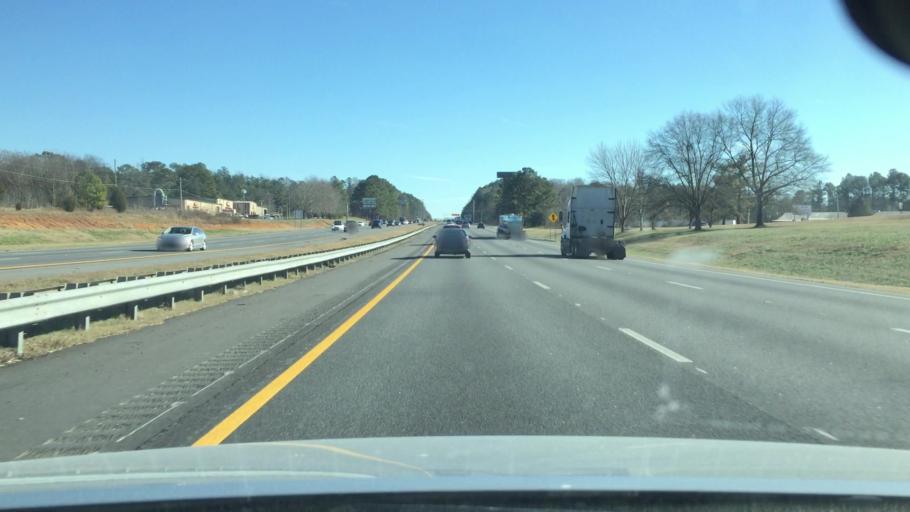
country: US
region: Georgia
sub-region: Catoosa County
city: Ringgold
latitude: 34.8920
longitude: -85.0739
